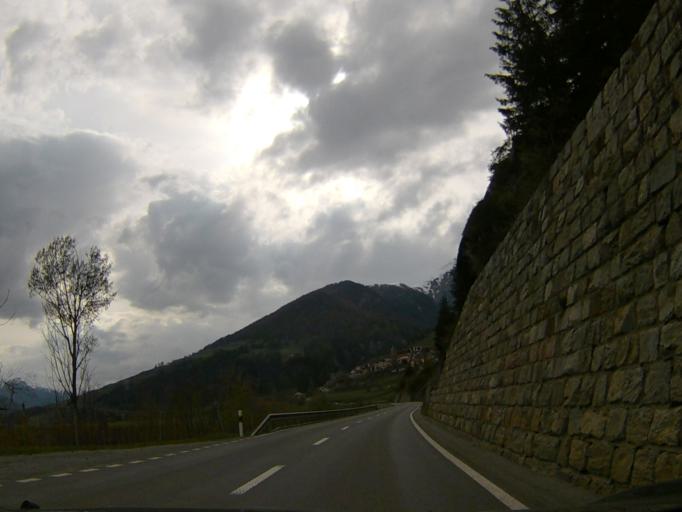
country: CH
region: Grisons
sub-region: Inn District
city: Scuol
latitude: 46.8340
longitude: 10.3987
